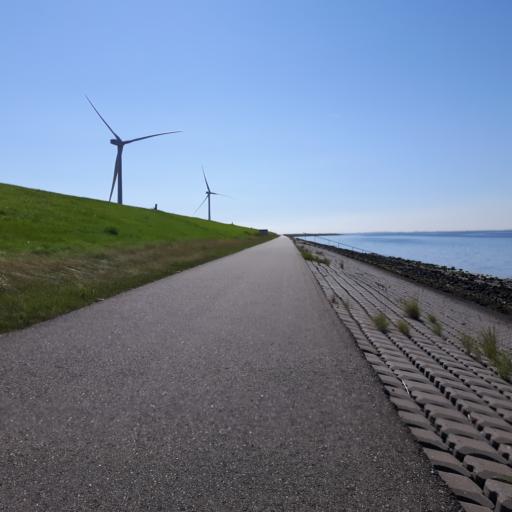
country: NL
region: Zeeland
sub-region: Gemeente Goes
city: Goes
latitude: 51.6338
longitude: 3.9406
